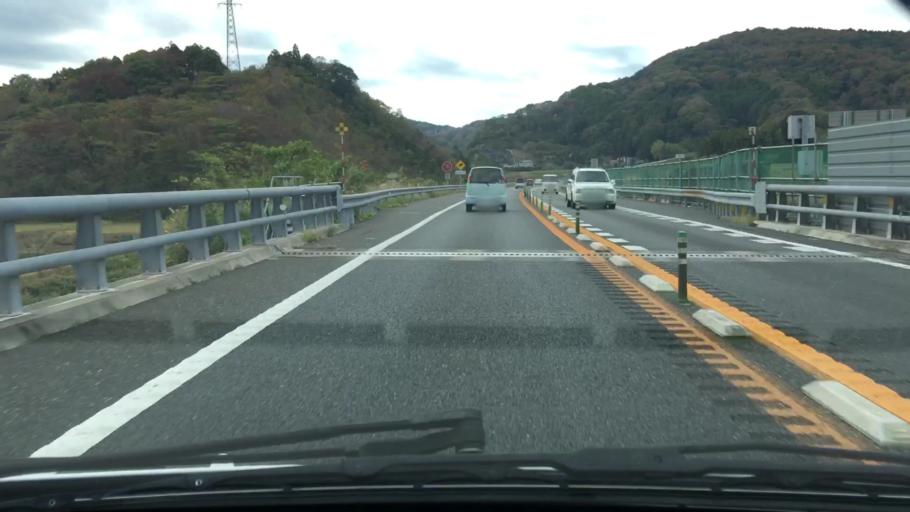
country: JP
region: Chiba
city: Futtsu
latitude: 35.2097
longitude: 139.8831
